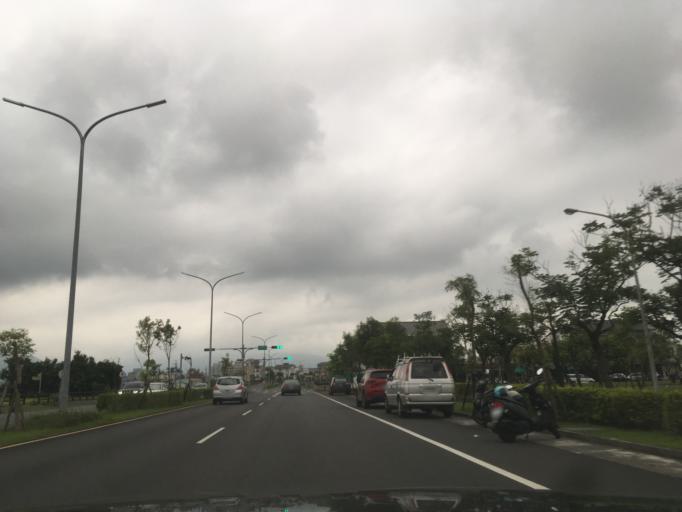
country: TW
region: Taiwan
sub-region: Yilan
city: Yilan
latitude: 24.7371
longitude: 121.7507
